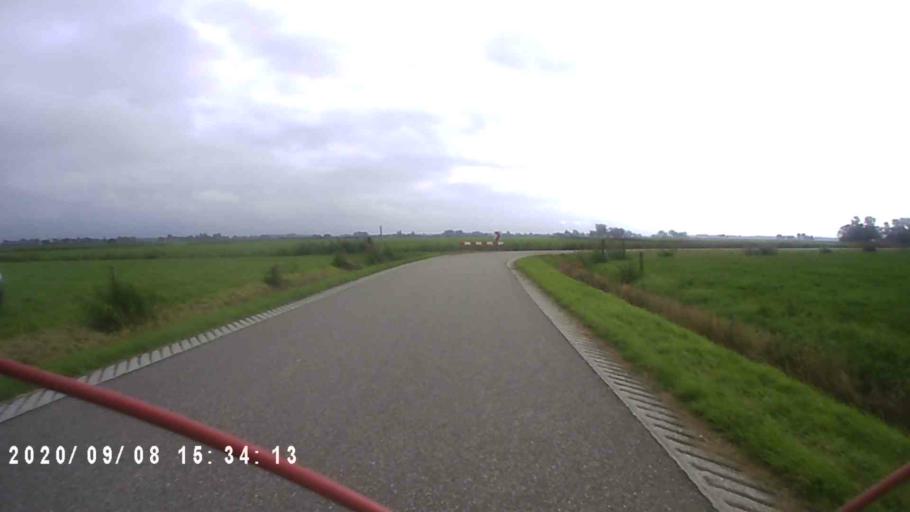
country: NL
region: Groningen
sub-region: Gemeente Bedum
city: Bedum
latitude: 53.2898
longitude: 6.6339
